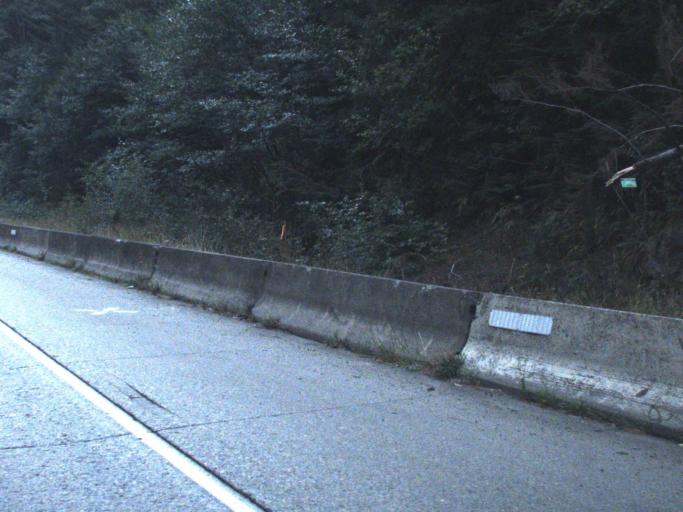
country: US
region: Washington
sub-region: King County
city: Tanner
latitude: 47.3950
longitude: -121.4604
